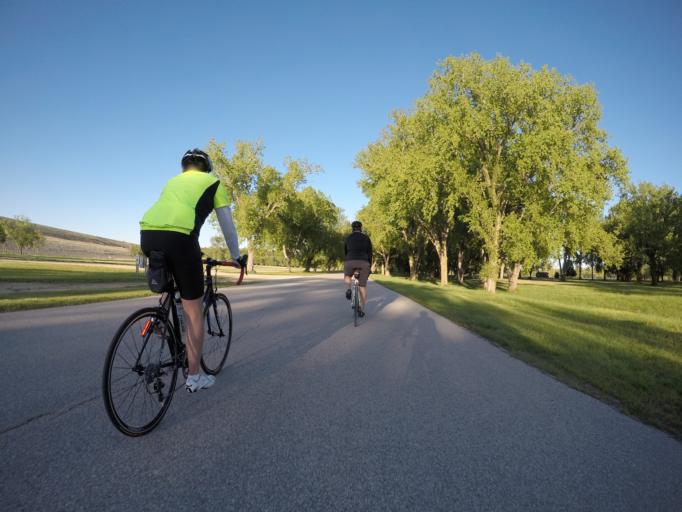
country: US
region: Kansas
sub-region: Riley County
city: Manhattan
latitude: 39.2553
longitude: -96.5881
